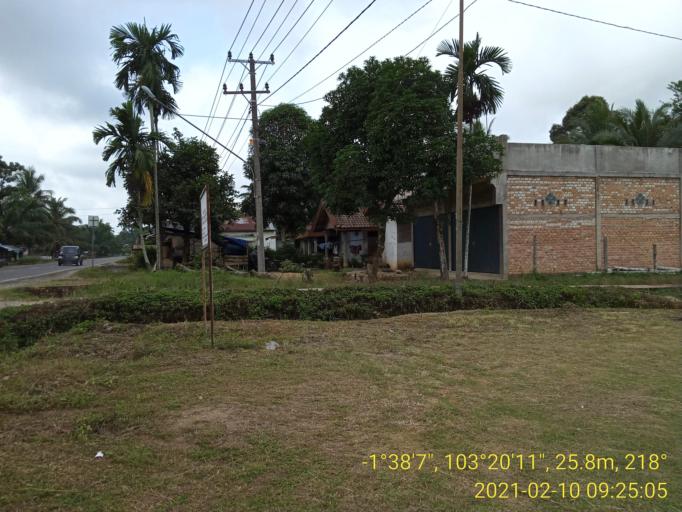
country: ID
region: Jambi
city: Muara Bulian
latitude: -1.6354
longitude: 103.3364
